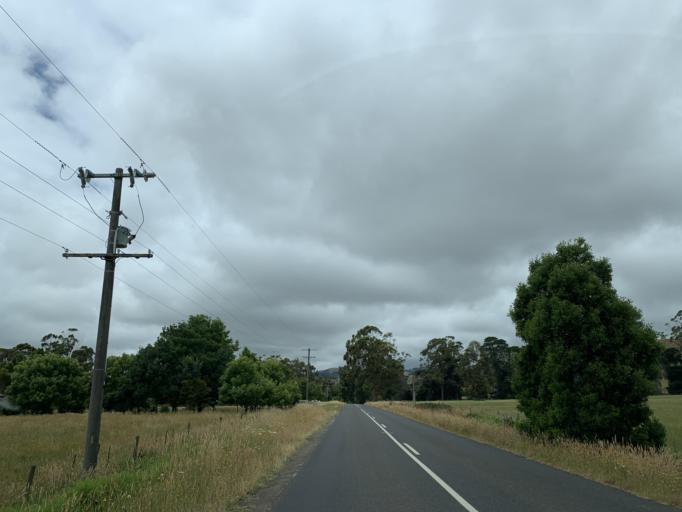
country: AU
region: Victoria
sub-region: Baw Baw
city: Warragul
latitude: -38.2448
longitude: 145.9832
